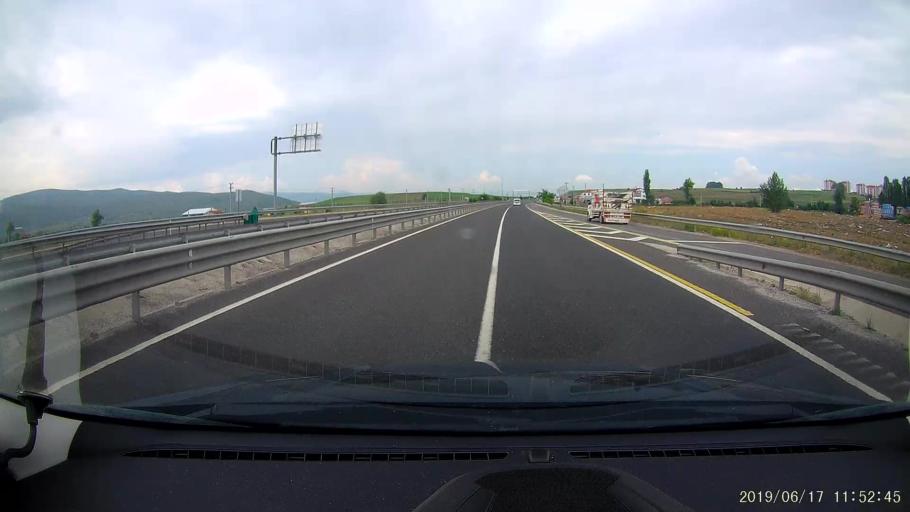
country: TR
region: Cankiri
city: Atkaracalar
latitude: 40.8072
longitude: 33.0759
